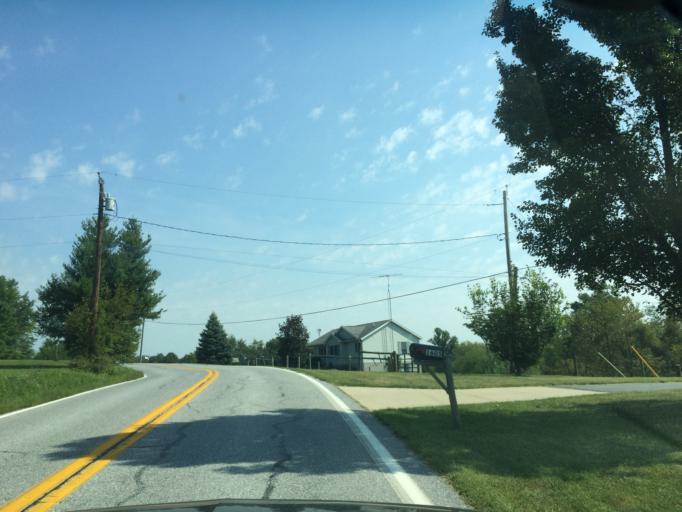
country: US
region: Maryland
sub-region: Carroll County
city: New Windsor
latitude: 39.6179
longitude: -77.1099
